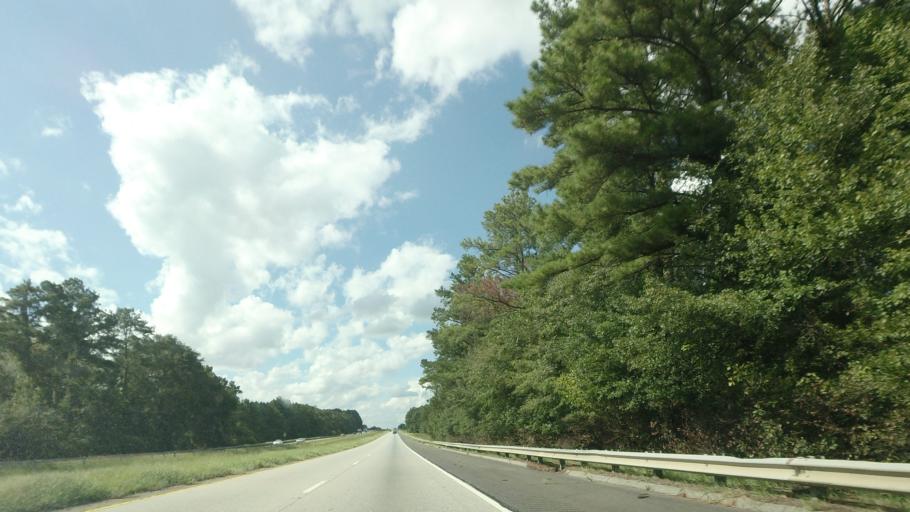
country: US
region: Georgia
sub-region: Bibb County
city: Macon
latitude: 32.7907
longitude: -83.5629
